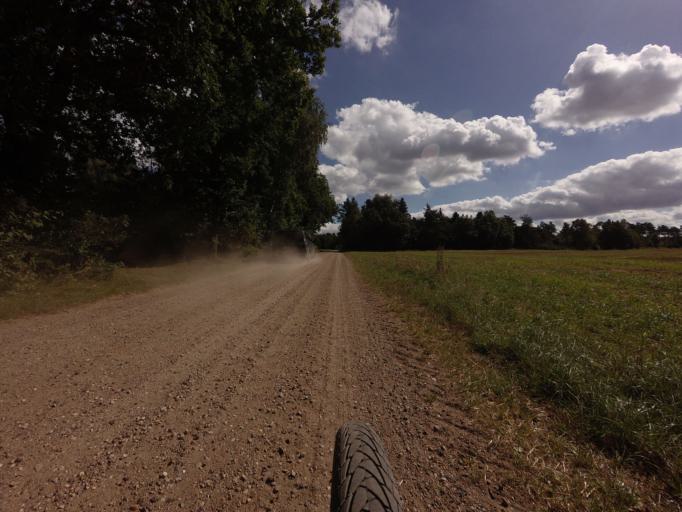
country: DK
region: Central Jutland
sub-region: Ikast-Brande Kommune
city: Brande
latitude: 55.9732
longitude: 9.1403
